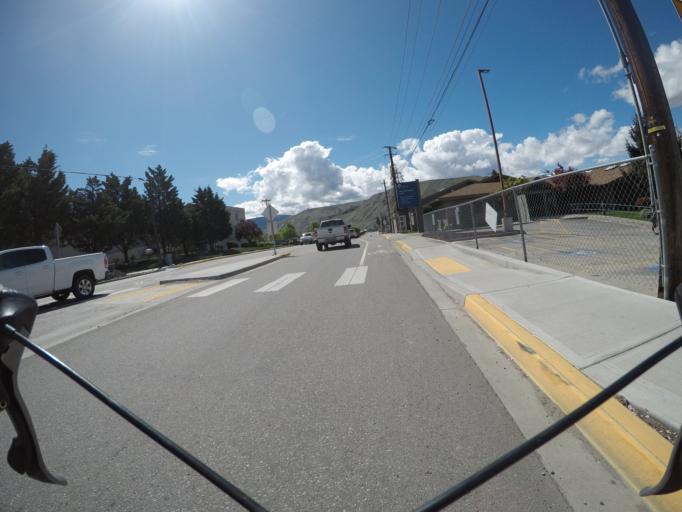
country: US
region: Washington
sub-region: Douglas County
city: East Wenatchee
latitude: 47.4047
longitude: -120.2820
